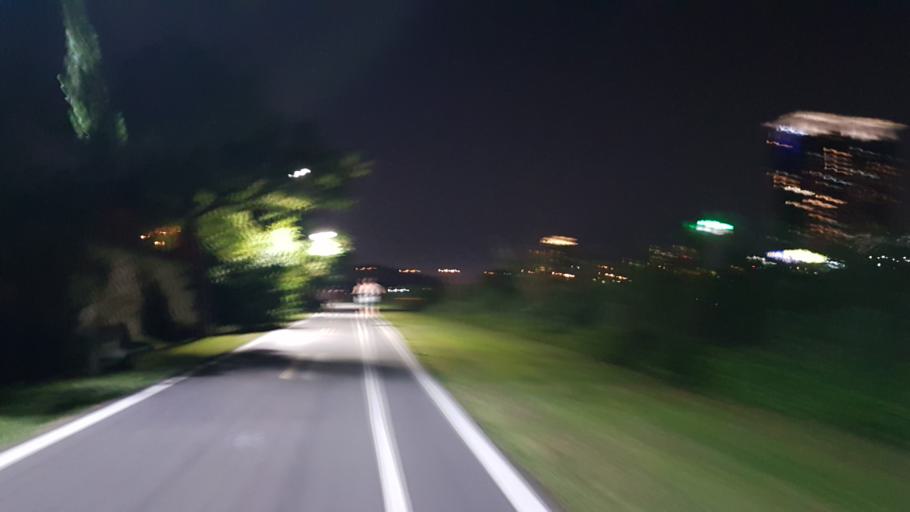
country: TW
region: Taipei
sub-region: Taipei
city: Banqiao
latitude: 24.9671
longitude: 121.5313
